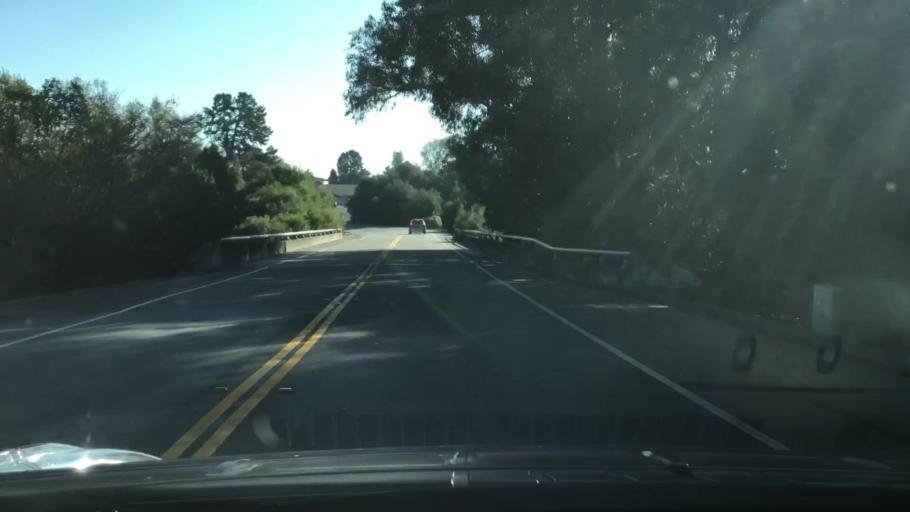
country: US
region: California
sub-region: Santa Clara County
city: Loyola
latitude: 37.3321
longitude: -122.0720
